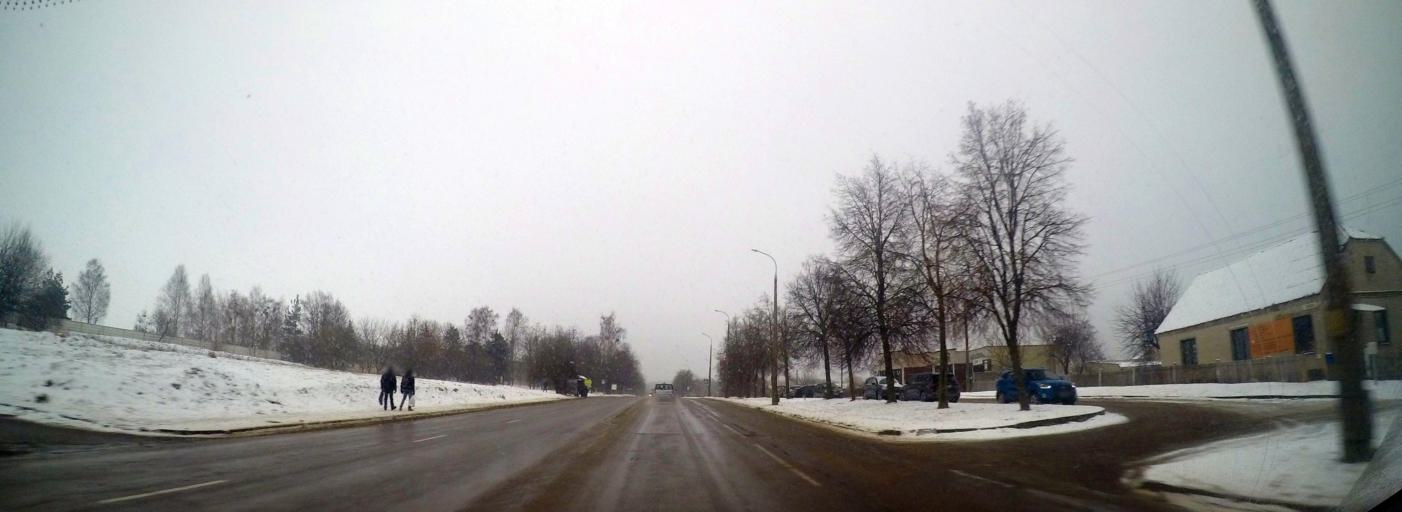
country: BY
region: Grodnenskaya
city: Hrodna
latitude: 53.6892
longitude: 23.8777
